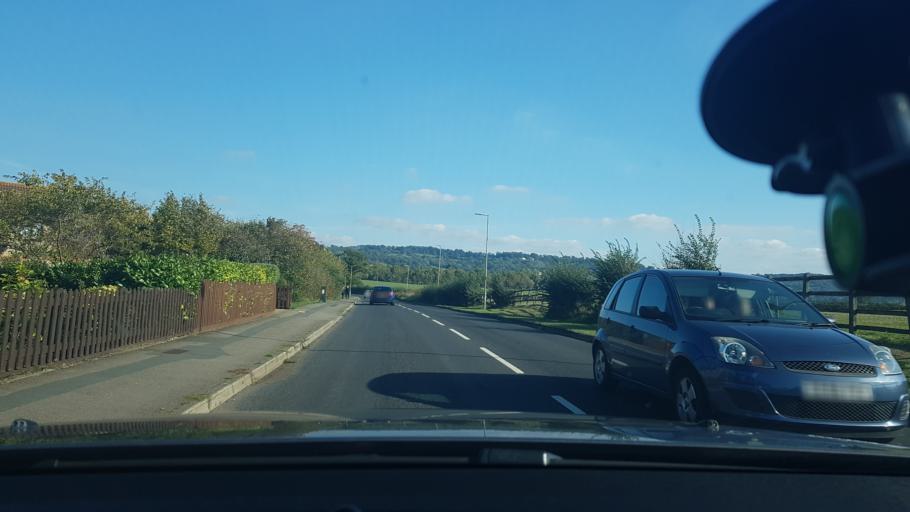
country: GB
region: England
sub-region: Gloucestershire
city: Gloucester
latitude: 51.8261
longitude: -2.2519
